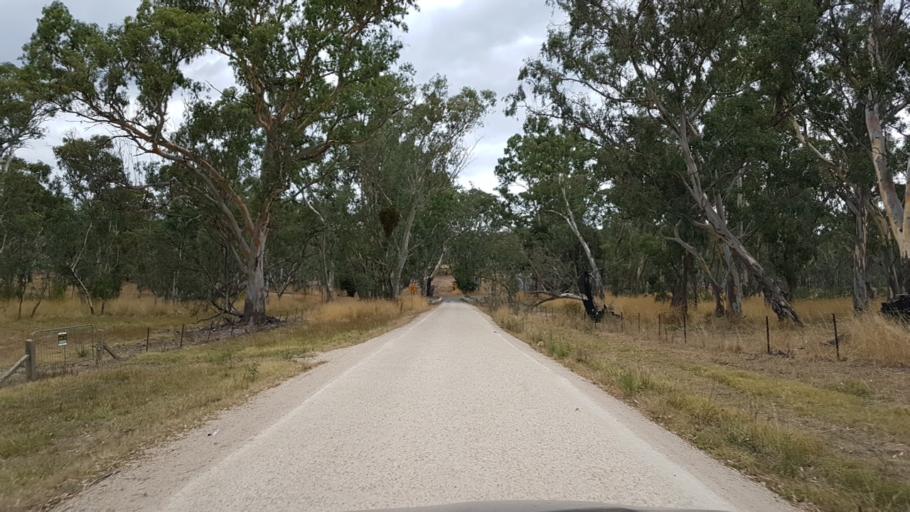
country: AU
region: South Australia
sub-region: Adelaide Hills
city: Gumeracha
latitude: -34.8087
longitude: 138.8352
